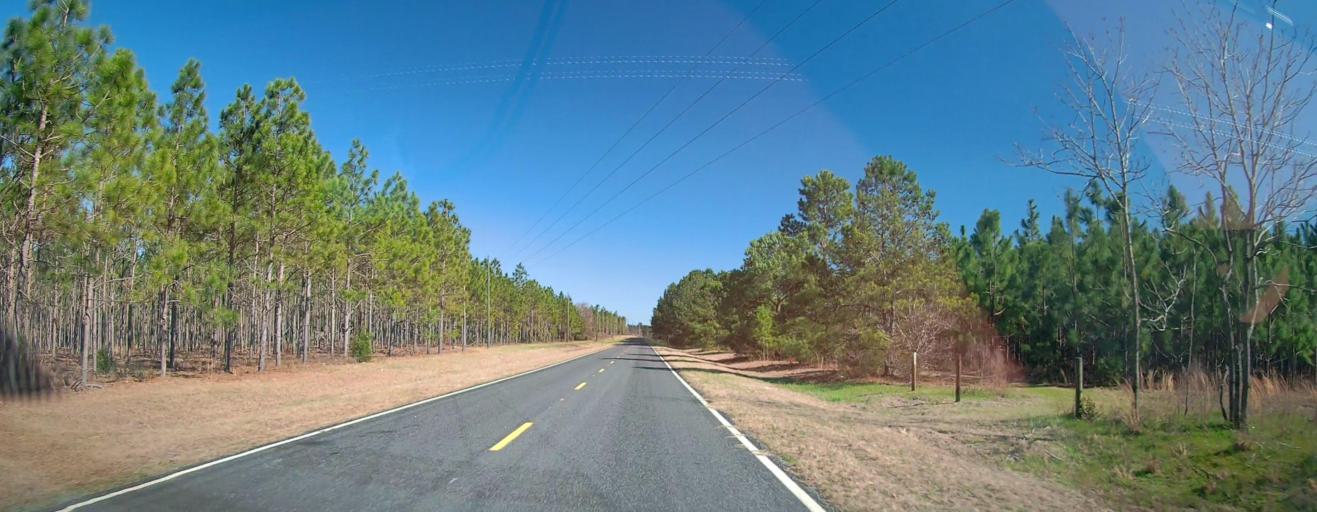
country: US
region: Georgia
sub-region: Macon County
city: Montezuma
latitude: 32.2799
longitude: -84.0202
